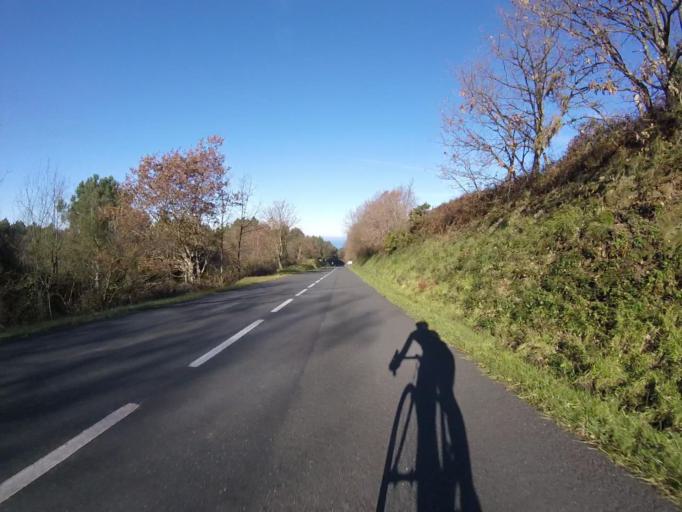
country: ES
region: Basque Country
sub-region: Provincia de Guipuzcoa
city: Fuenterrabia
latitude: 43.3674
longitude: -1.8312
